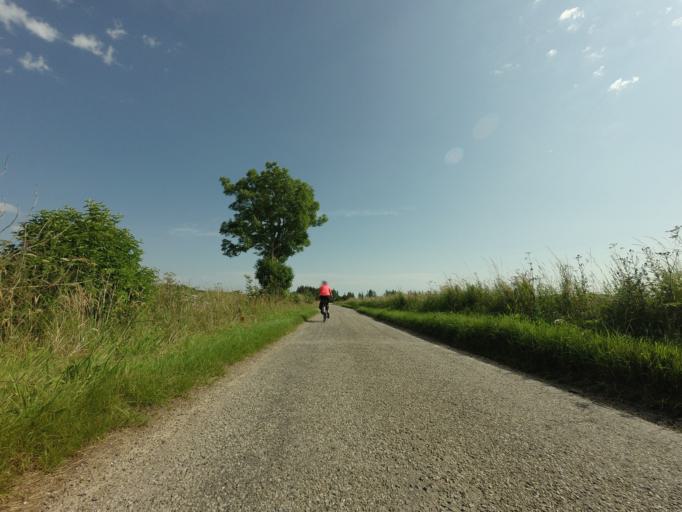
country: GB
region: Scotland
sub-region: Highland
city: Invergordon
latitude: 57.7241
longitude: -4.1994
